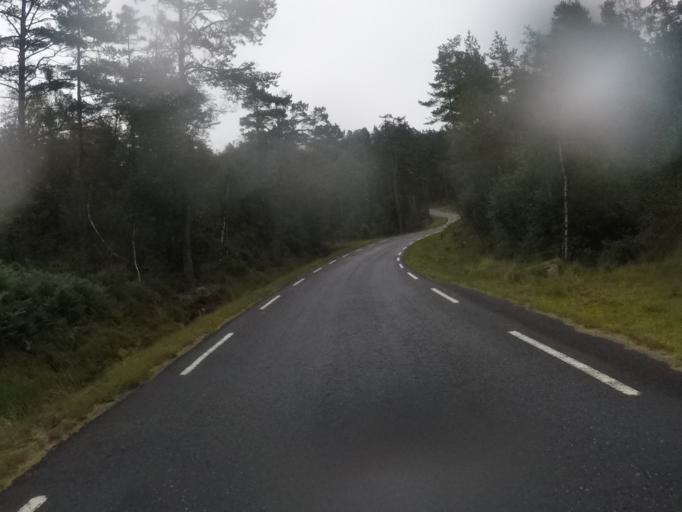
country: NO
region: Vest-Agder
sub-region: Kvinesdal
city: Liknes
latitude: 58.2579
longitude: 7.0285
